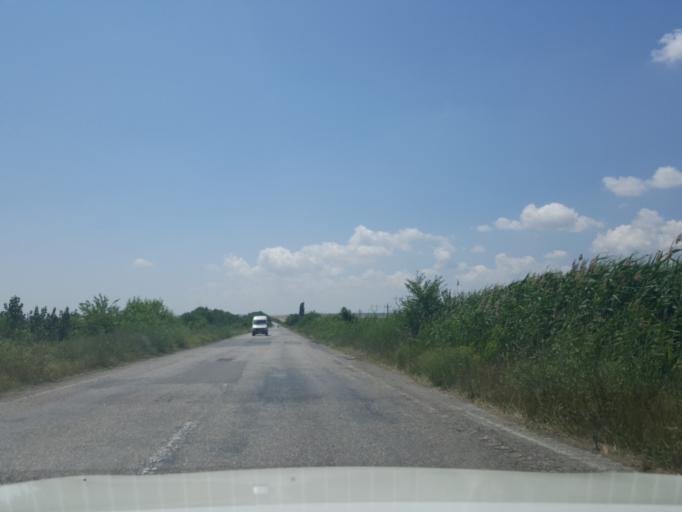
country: UA
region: Odessa
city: Starokozache
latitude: 46.4028
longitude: 30.1016
